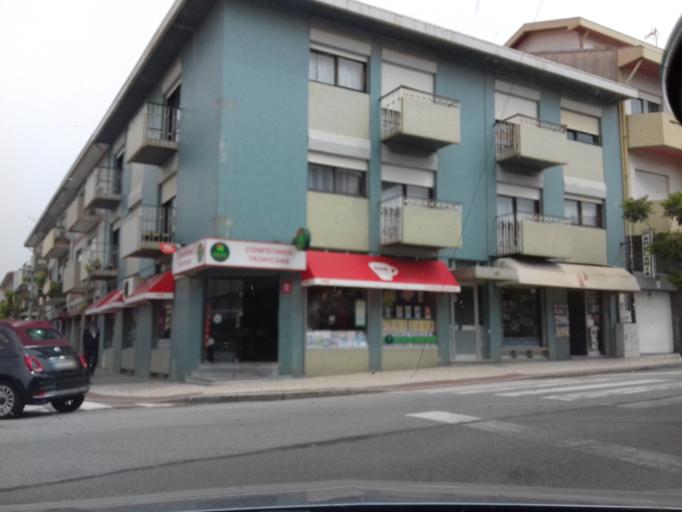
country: PT
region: Aveiro
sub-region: Espinho
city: Espinho
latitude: 41.0085
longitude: -8.6362
